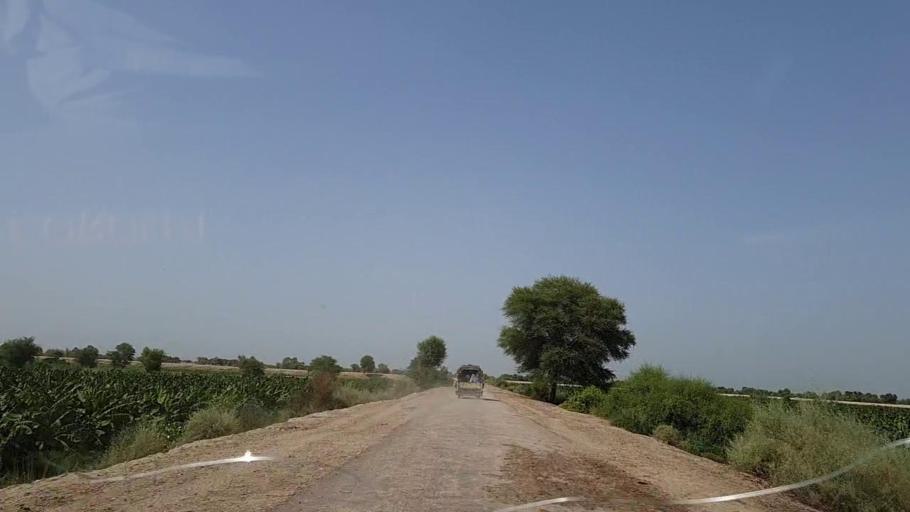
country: PK
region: Sindh
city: Kandiaro
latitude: 27.0530
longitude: 68.1349
